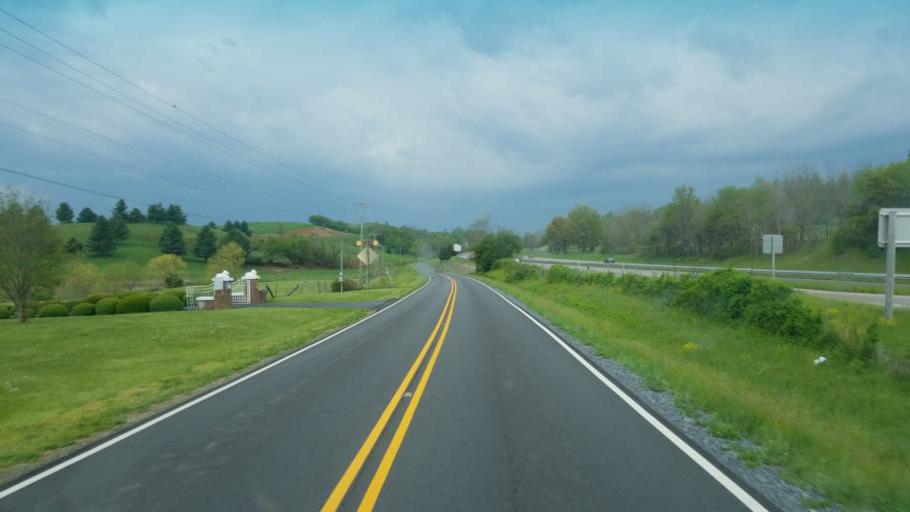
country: US
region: Virginia
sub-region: Washington County
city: Glade Spring
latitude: 36.7819
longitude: -81.7361
